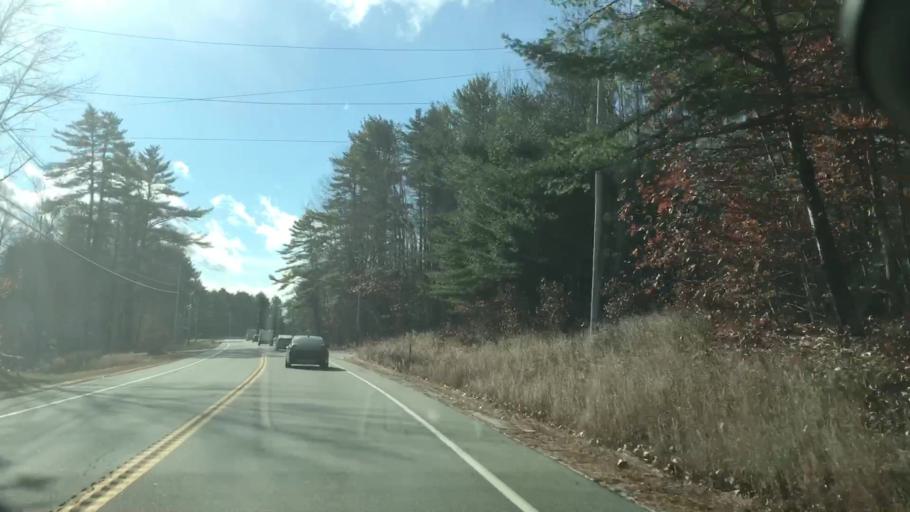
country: US
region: New Hampshire
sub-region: Carroll County
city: Wolfeboro
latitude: 43.6149
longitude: -71.1757
